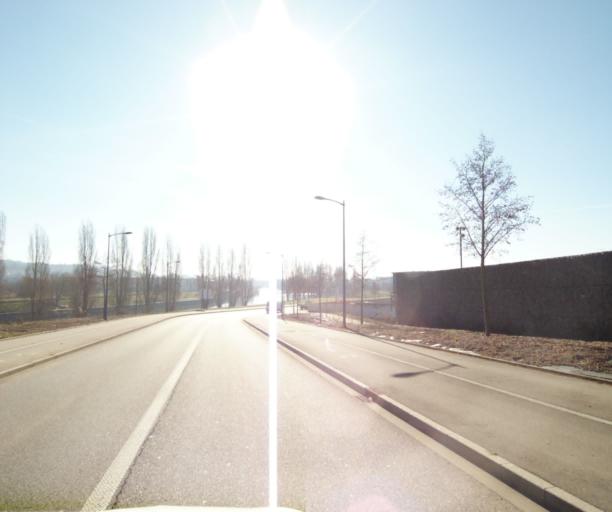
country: FR
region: Lorraine
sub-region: Departement de Meurthe-et-Moselle
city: Maxeville
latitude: 48.7165
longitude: 6.1721
